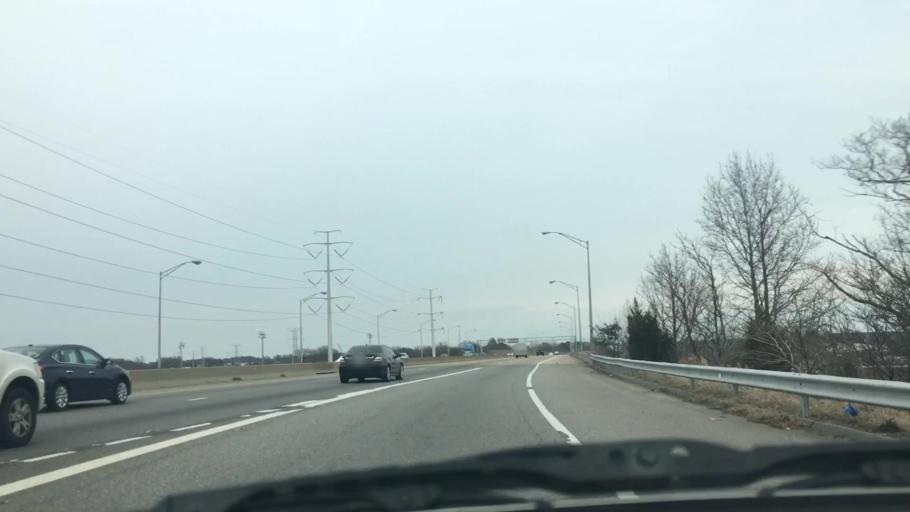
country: US
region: Virginia
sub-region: City of Newport News
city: Newport News
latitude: 36.9909
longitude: -76.4246
